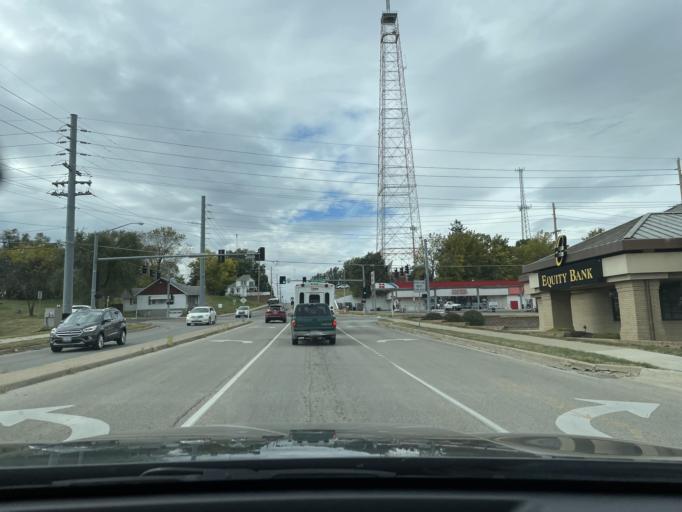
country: US
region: Missouri
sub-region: Buchanan County
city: Saint Joseph
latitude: 39.7698
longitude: -94.7958
